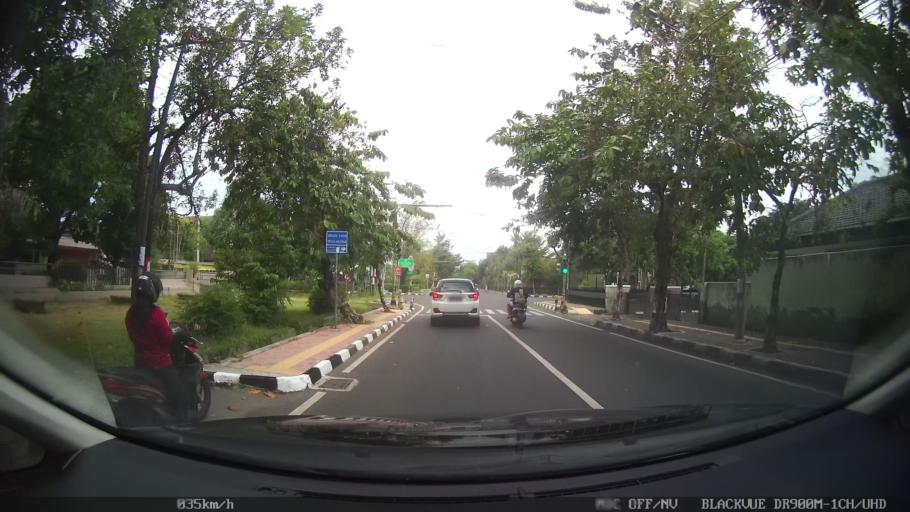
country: ID
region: Daerah Istimewa Yogyakarta
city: Yogyakarta
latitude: -7.7920
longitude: 110.3932
